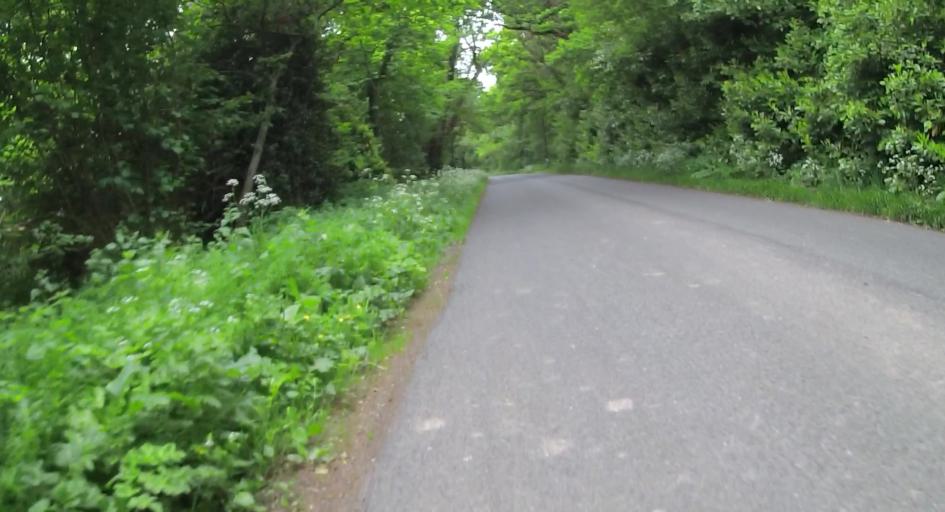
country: GB
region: England
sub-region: West Berkshire
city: Stratfield Mortimer
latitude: 51.3681
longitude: -1.0319
